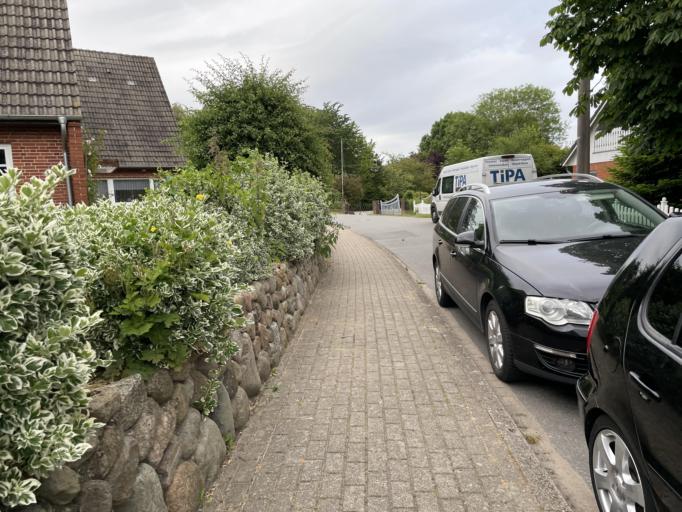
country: DE
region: Schleswig-Holstein
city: Mildstedt
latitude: 54.4597
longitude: 9.0923
